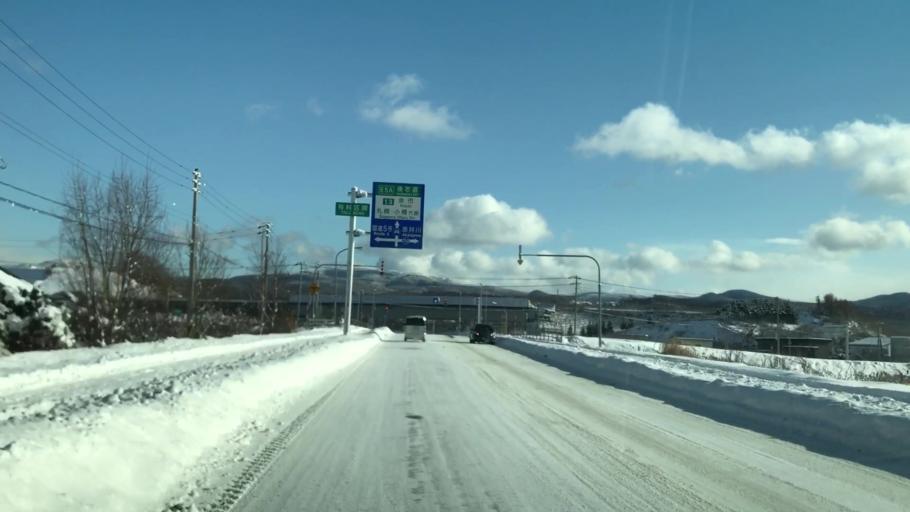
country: JP
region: Hokkaido
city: Yoichi
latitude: 43.1820
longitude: 140.8197
